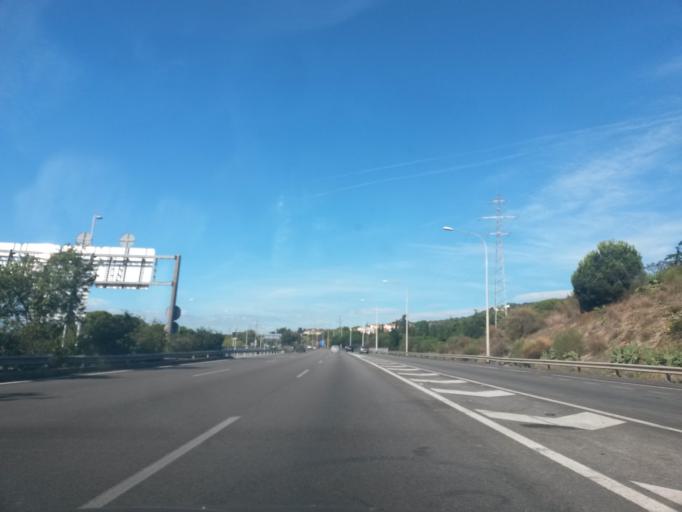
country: ES
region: Catalonia
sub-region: Provincia de Barcelona
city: Premia de Mar
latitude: 41.5055
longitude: 2.3621
